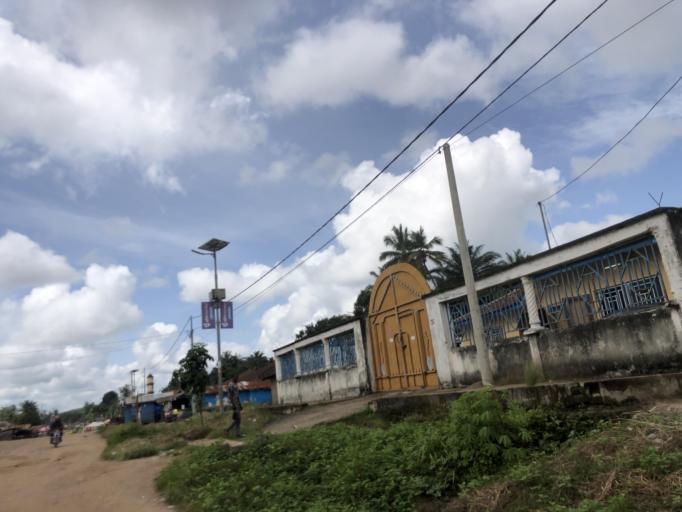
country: SL
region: Northern Province
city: Makeni
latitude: 8.8688
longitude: -12.0539
